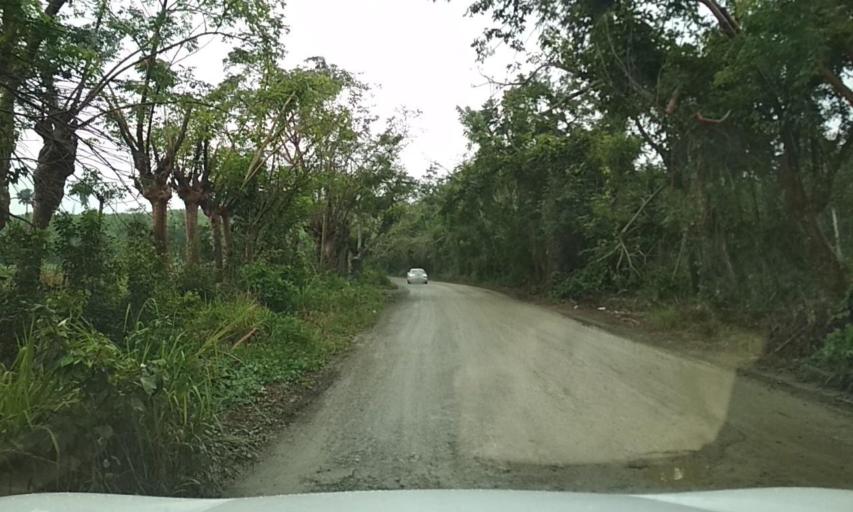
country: MX
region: Veracruz
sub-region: Coatzintla
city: Manuel Maria Contreras
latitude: 20.4600
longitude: -97.4738
